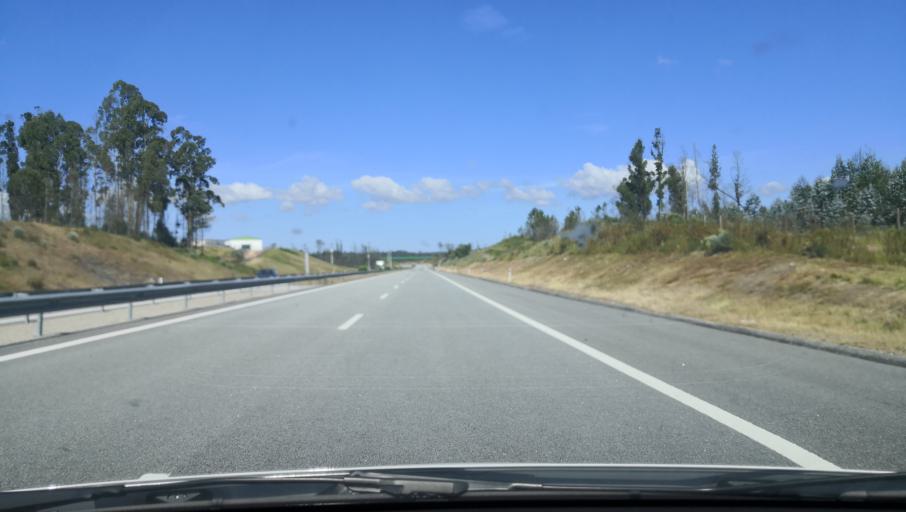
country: PT
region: Coimbra
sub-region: Cantanhede
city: Cantanhede
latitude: 40.2848
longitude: -8.5592
